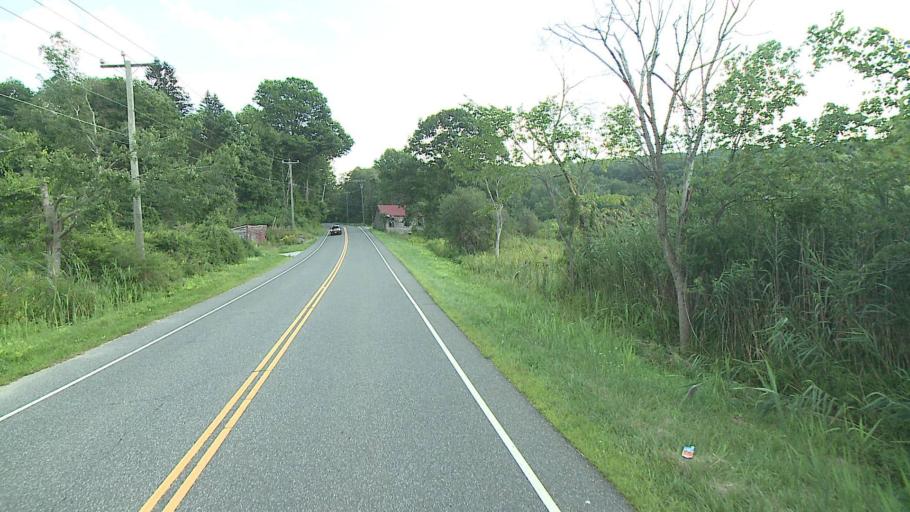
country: US
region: Connecticut
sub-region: Litchfield County
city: Bethlehem Village
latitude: 41.6780
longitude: -73.2470
